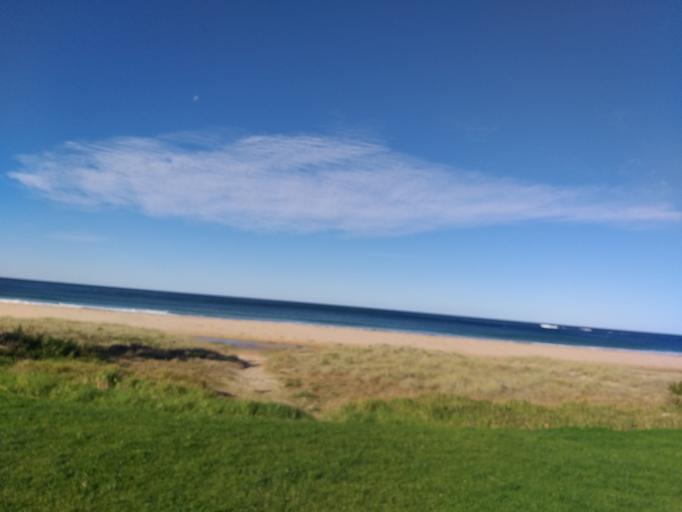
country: AU
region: New South Wales
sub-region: Wollongong
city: Bulli
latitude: -34.3350
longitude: 150.9240
